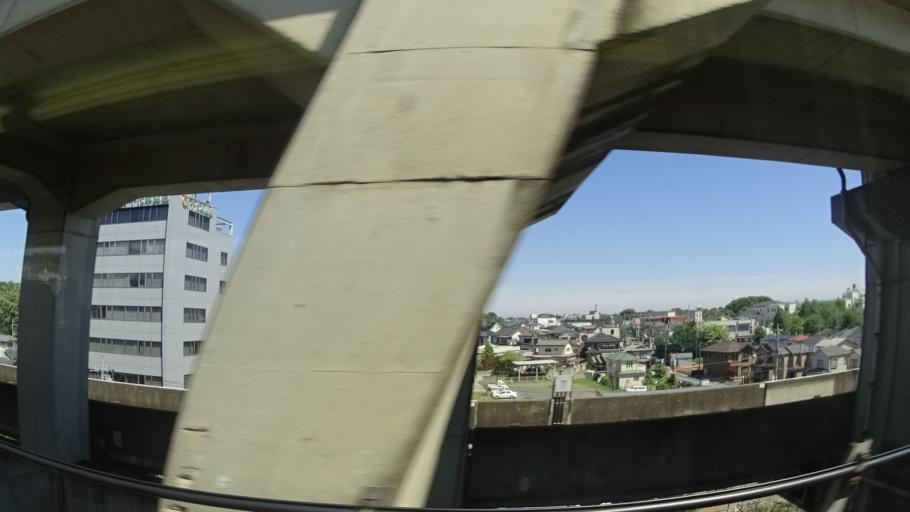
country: JP
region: Saitama
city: Ageoshimo
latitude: 35.9691
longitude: 139.6233
